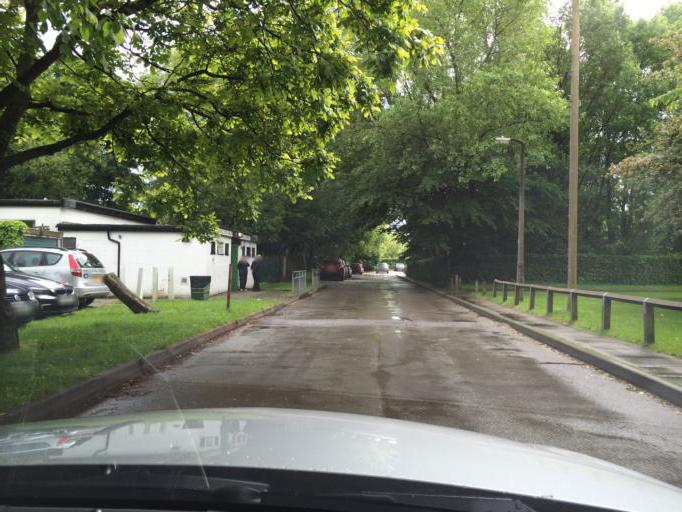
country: GB
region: England
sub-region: Trafford
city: Sale
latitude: 53.4154
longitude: -2.3304
